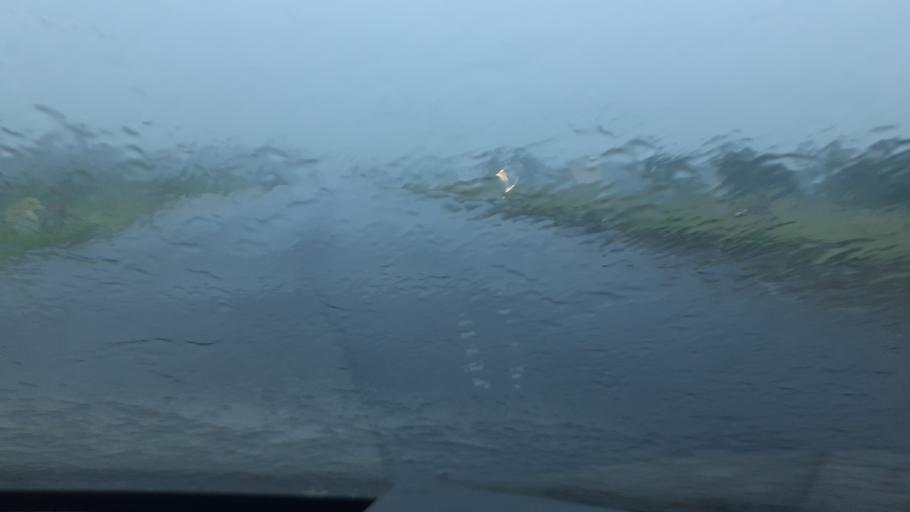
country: IN
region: Tamil Nadu
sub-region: Virudhunagar
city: Virudunagar
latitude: 9.4992
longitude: 77.9416
